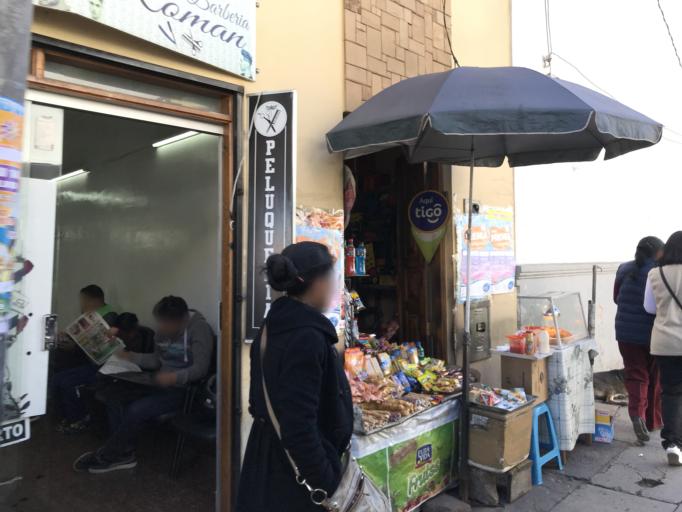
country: BO
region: Chuquisaca
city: Sucre
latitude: -19.0431
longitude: -65.2579
